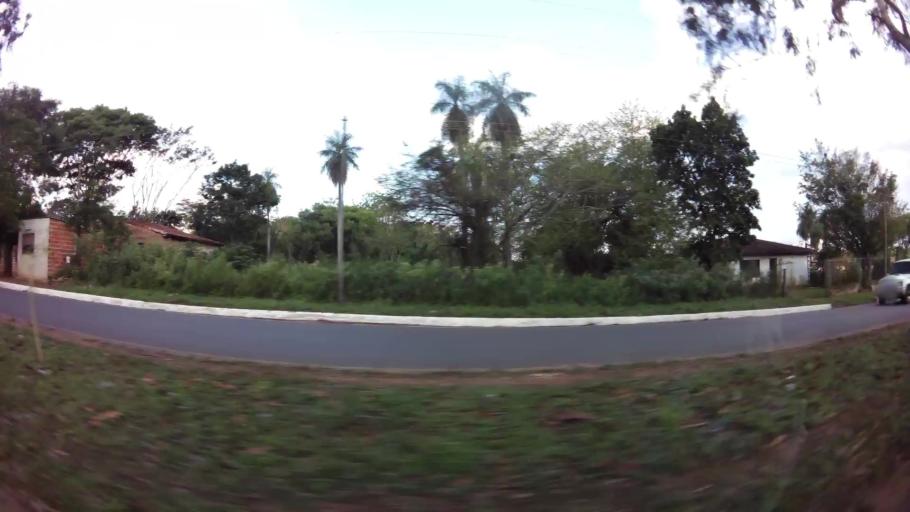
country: PY
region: Central
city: Nemby
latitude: -25.3688
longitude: -57.5244
